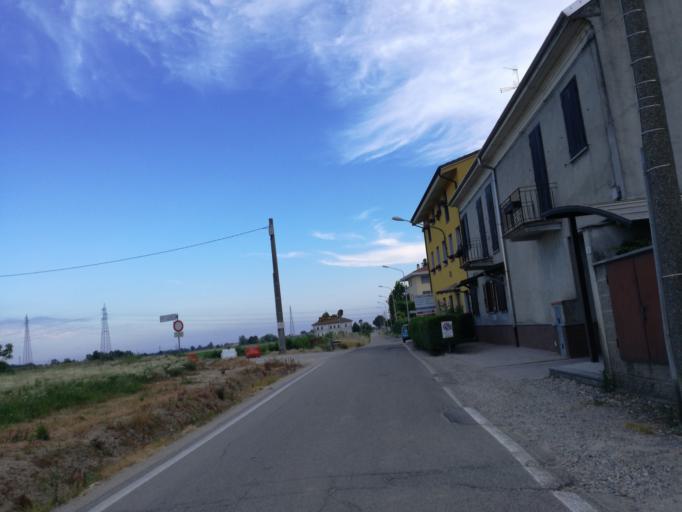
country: IT
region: Piedmont
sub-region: Provincia di Novara
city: Torrion Quartara
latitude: 45.4178
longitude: 8.6191
